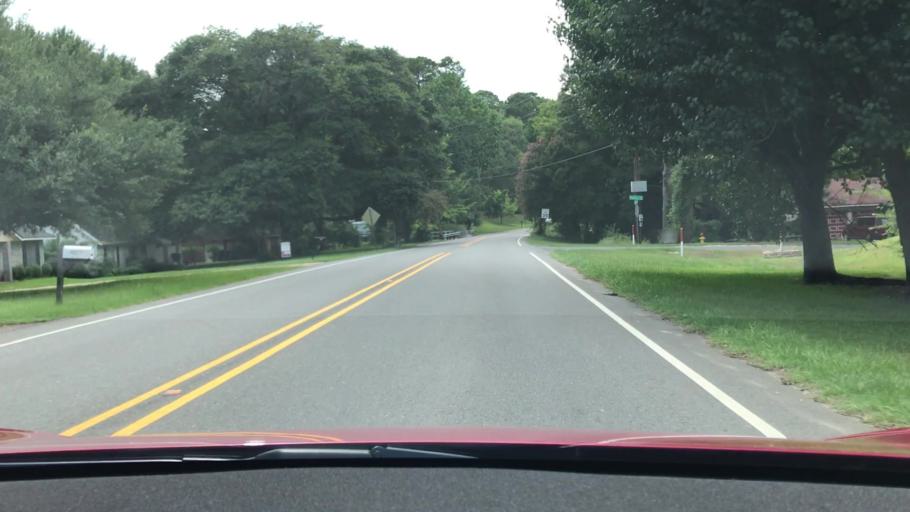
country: US
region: Louisiana
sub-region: De Soto Parish
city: Stonewall
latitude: 32.3891
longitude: -93.7905
